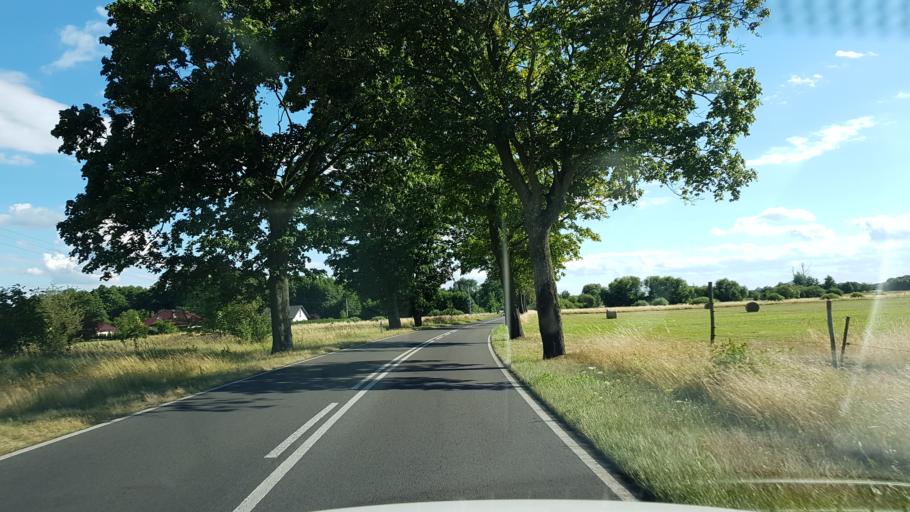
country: PL
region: West Pomeranian Voivodeship
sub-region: Powiat goleniowski
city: Goleniow
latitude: 53.5903
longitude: 14.7405
